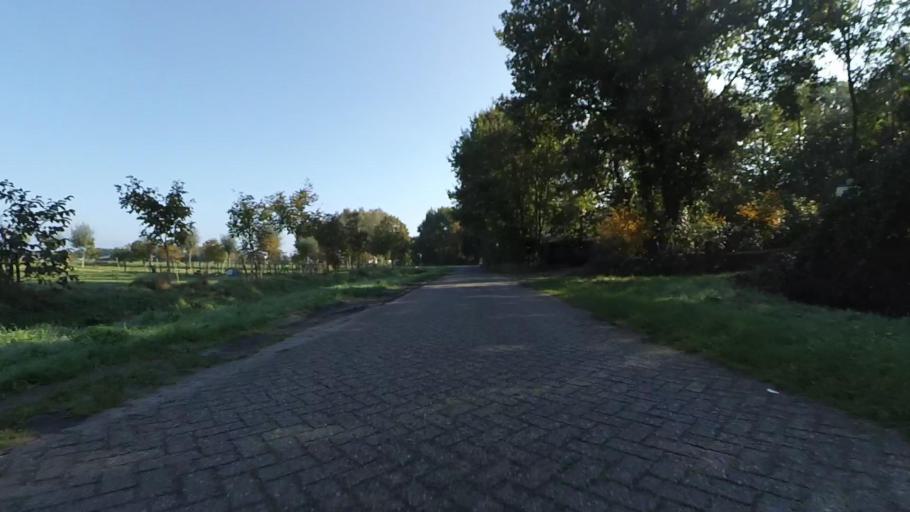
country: NL
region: Gelderland
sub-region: Gemeente Nijkerk
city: Nijkerk
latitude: 52.2504
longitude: 5.5428
